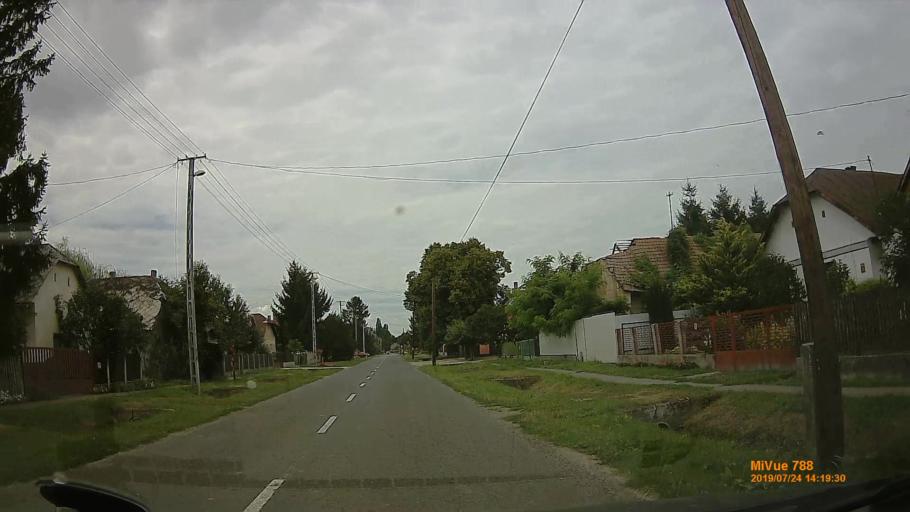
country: HU
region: Szabolcs-Szatmar-Bereg
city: Mandok
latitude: 48.3194
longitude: 22.2694
